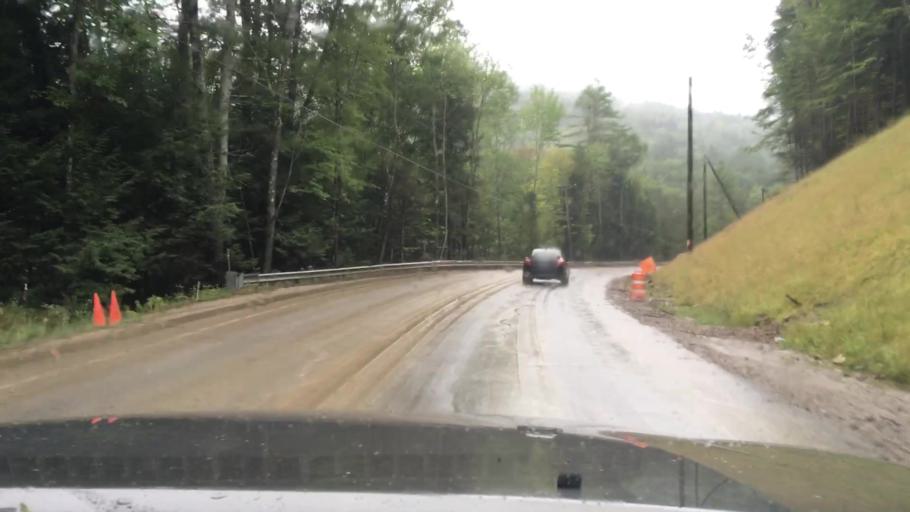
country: US
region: New Hampshire
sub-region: Cheshire County
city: Marlborough
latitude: 42.9769
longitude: -72.2051
